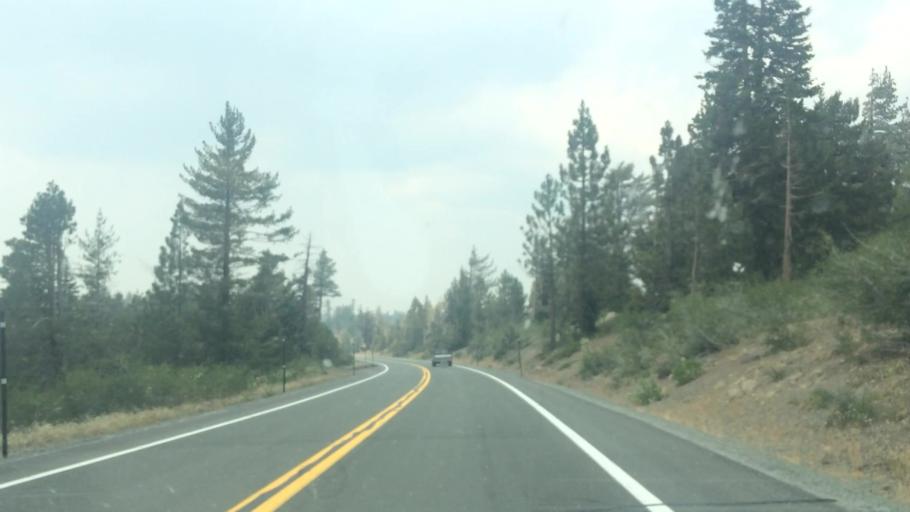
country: US
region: California
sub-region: El Dorado County
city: South Lake Tahoe
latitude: 38.6327
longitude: -120.1639
